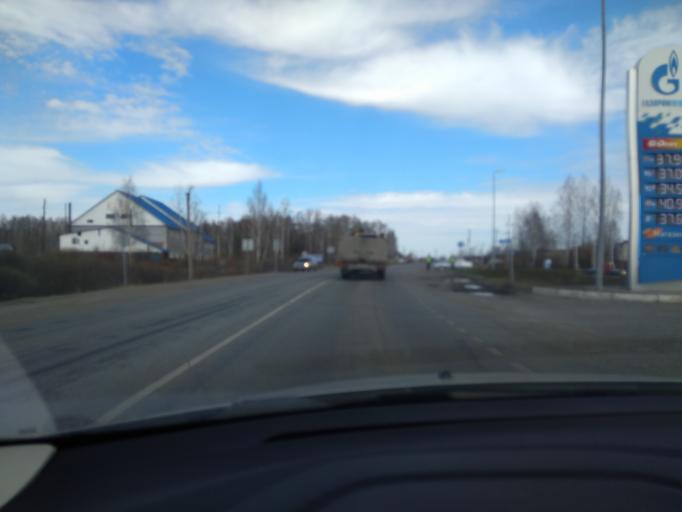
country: RU
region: Sverdlovsk
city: Pyshma
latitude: 56.9519
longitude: 63.2278
